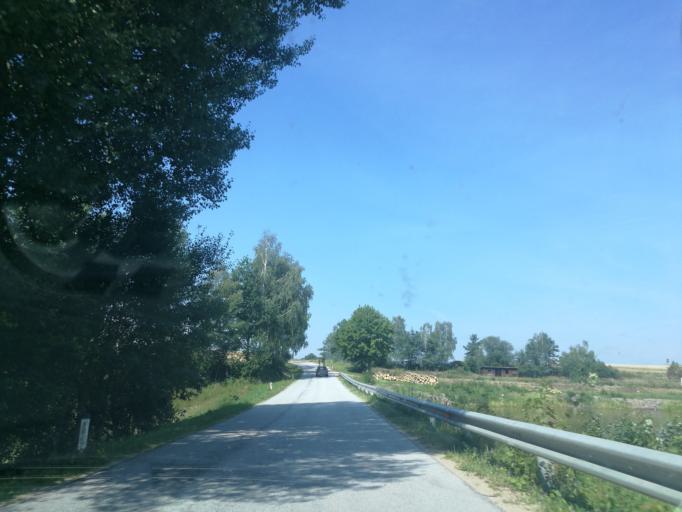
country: AT
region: Lower Austria
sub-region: Politischer Bezirk Gmund
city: Reingers
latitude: 48.9483
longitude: 15.0933
